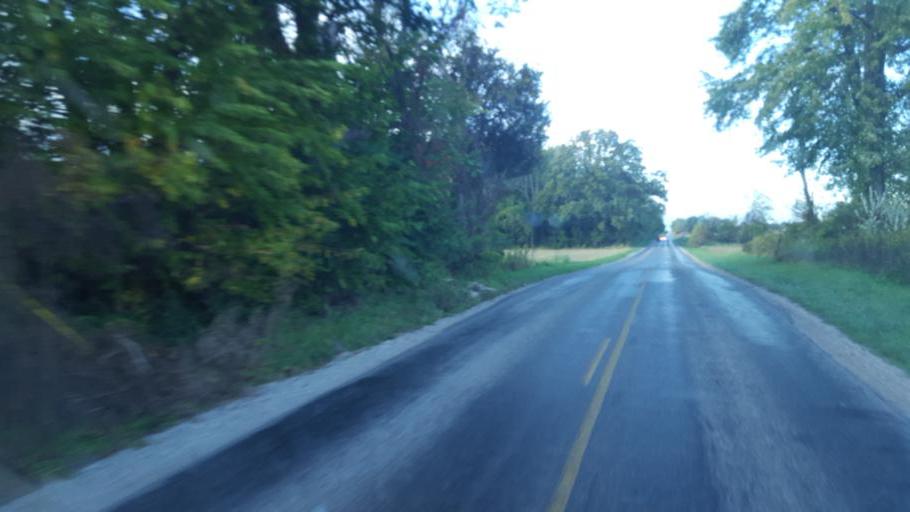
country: US
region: Ohio
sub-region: Franklin County
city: New Albany
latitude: 40.0564
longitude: -82.7552
